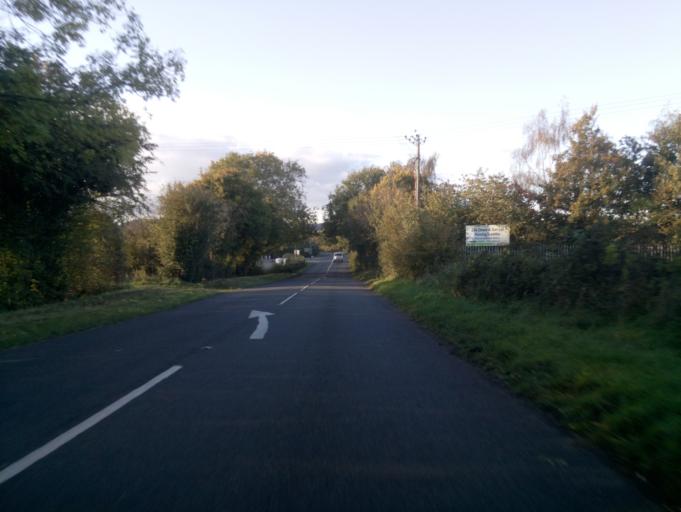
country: GB
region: England
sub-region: Worcestershire
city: Great Malvern
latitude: 52.0166
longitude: -2.3180
